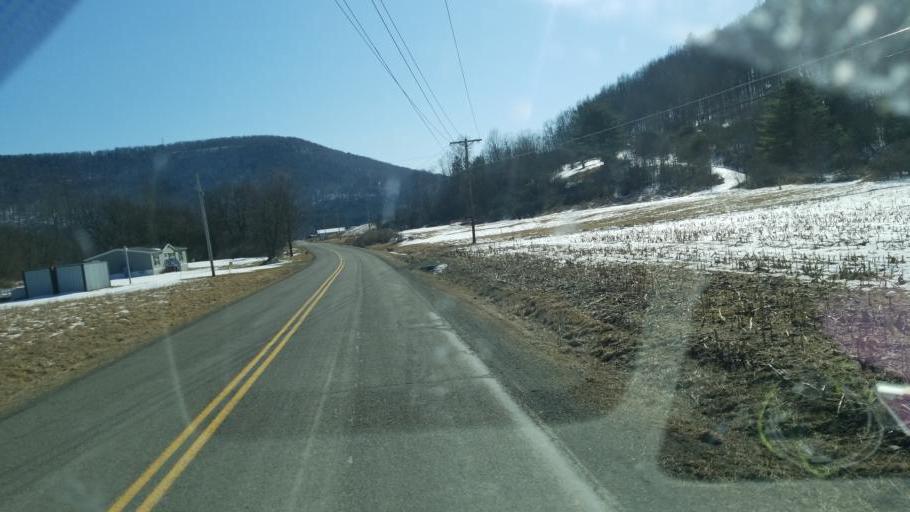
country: US
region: Pennsylvania
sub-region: Tioga County
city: Westfield
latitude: 41.9263
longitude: -77.5654
